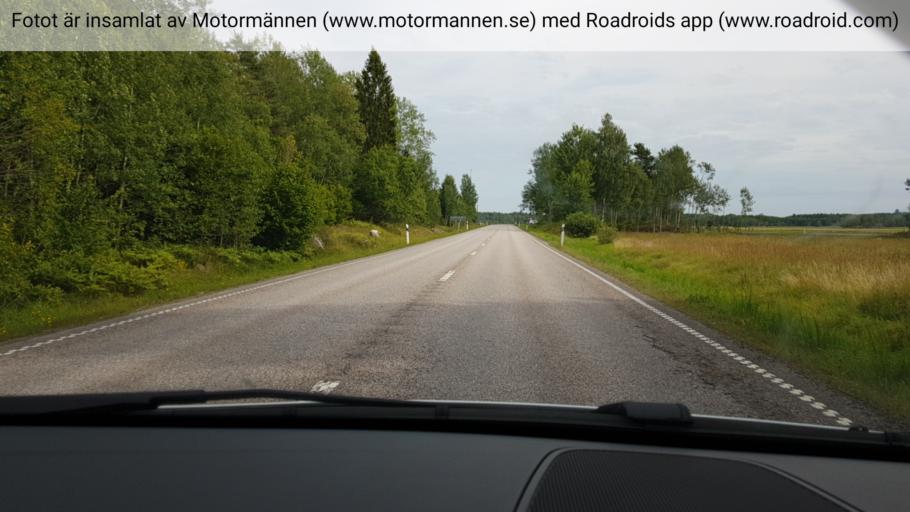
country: SE
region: Stockholm
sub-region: Norrtalje Kommun
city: Hallstavik
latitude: 60.0432
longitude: 18.5395
